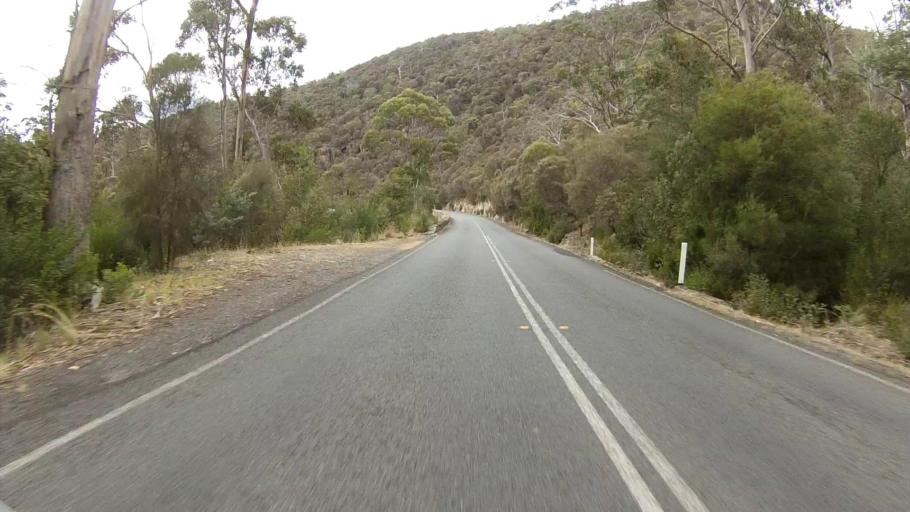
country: AU
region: Tasmania
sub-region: Sorell
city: Sorell
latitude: -42.5599
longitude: 147.8505
